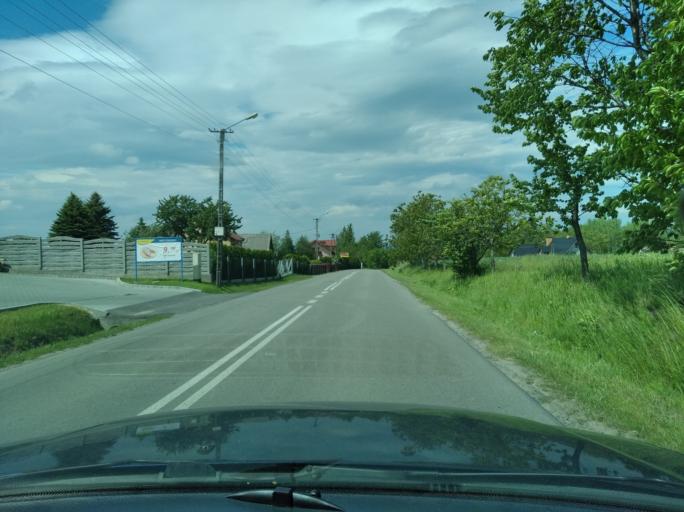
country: PL
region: Subcarpathian Voivodeship
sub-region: Powiat ropczycko-sedziszowski
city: Ropczyce
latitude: 50.0351
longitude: 21.6197
